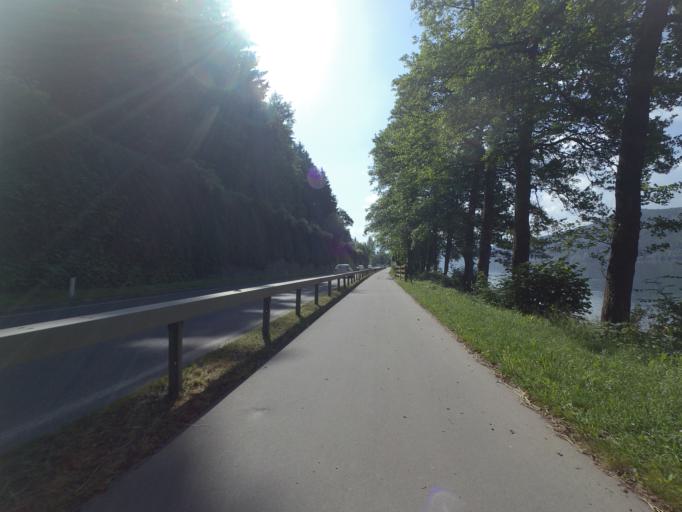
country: AT
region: Carinthia
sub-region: Politischer Bezirk Spittal an der Drau
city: Seeboden
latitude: 46.8124
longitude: 13.5445
